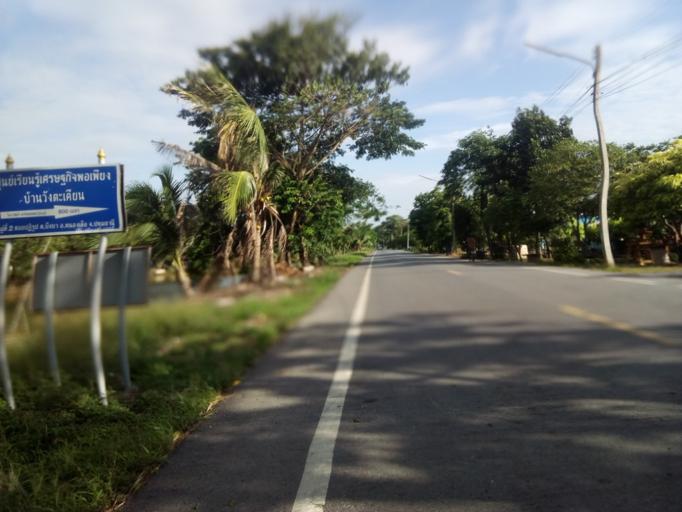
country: TH
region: Pathum Thani
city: Nong Suea
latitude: 14.1094
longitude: 100.8461
